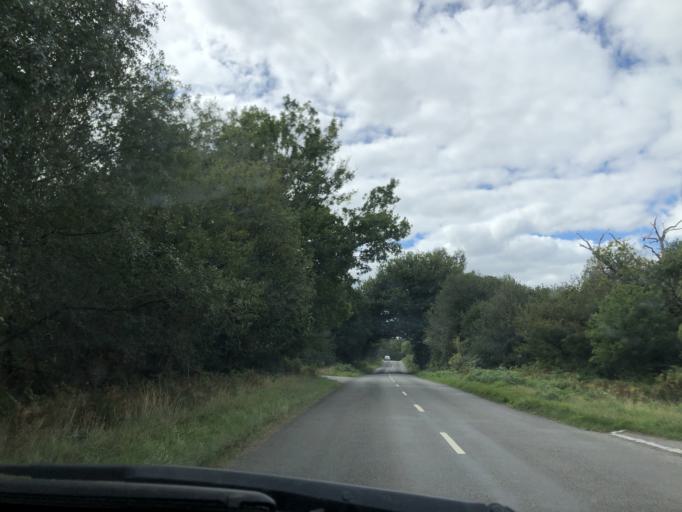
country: GB
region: England
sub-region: East Sussex
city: Forest Row
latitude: 51.0738
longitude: 0.0552
